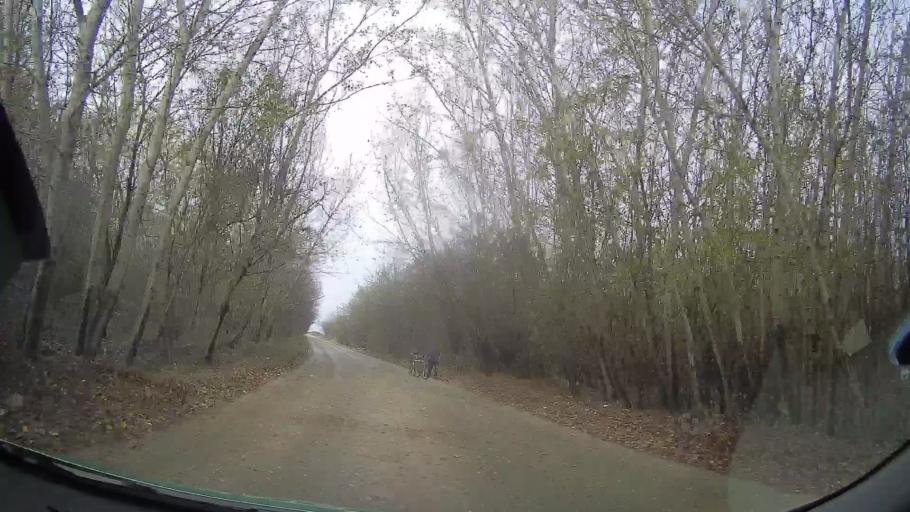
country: RO
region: Ialomita
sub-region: Comuna Fierbinti-Targ
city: Fierbinti-Targ
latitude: 44.6821
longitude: 26.3486
